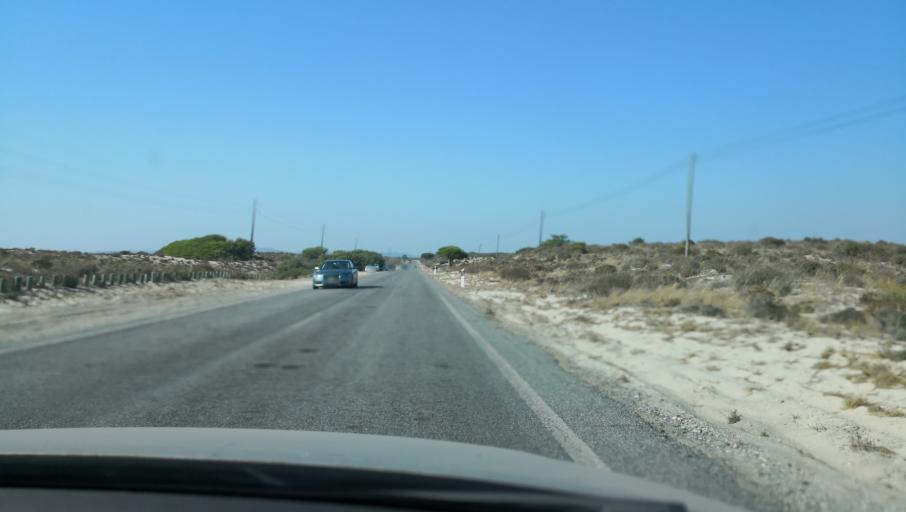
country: PT
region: Setubal
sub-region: Setubal
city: Setubal
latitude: 38.4254
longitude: -8.8236
